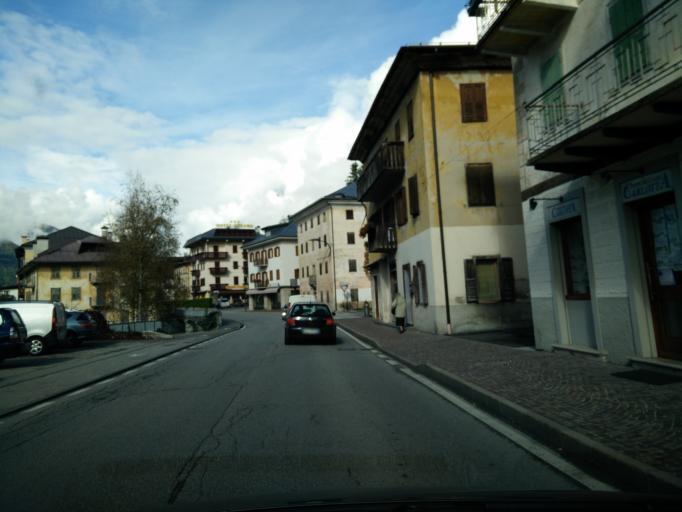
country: IT
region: Veneto
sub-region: Provincia di Belluno
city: Auronzo
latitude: 46.5475
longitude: 12.4524
